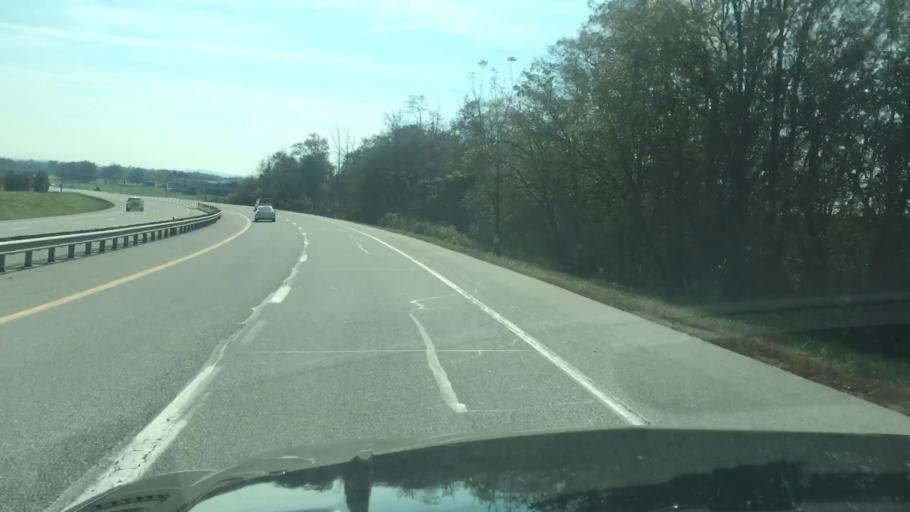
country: US
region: Pennsylvania
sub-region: Cumberland County
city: Mechanicsburg
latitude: 40.2642
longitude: -77.0423
